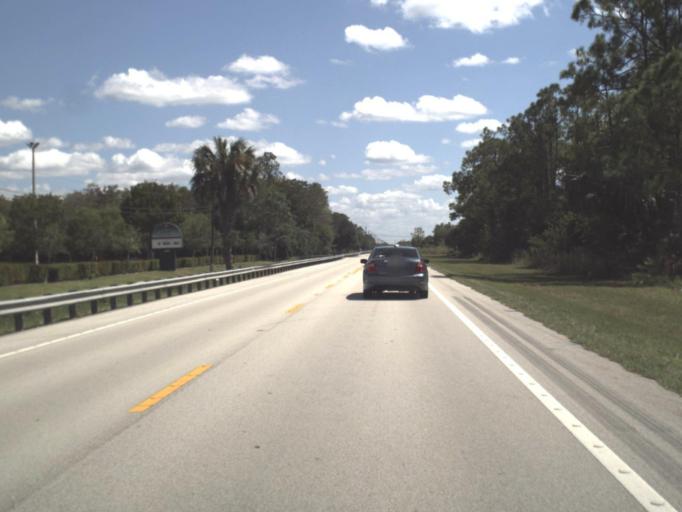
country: US
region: Florida
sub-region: Collier County
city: Lely Resort
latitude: 26.0221
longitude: -81.6347
